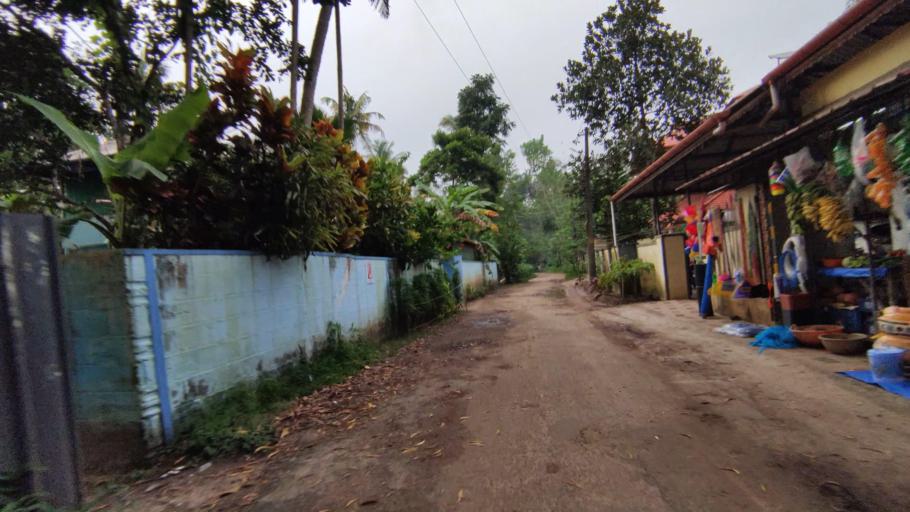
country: IN
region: Kerala
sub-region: Alappuzha
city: Shertallai
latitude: 9.6415
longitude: 76.3636
